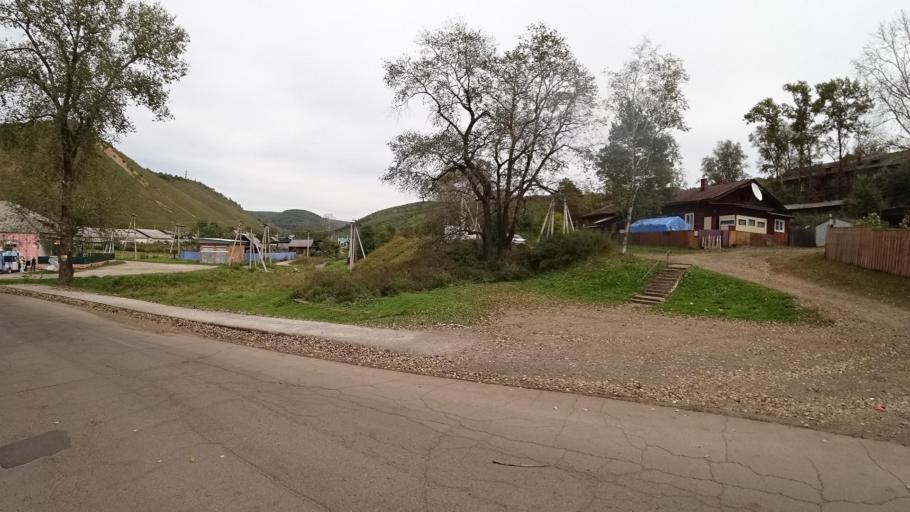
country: RU
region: Jewish Autonomous Oblast
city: Khingansk
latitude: 49.0189
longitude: 131.0631
